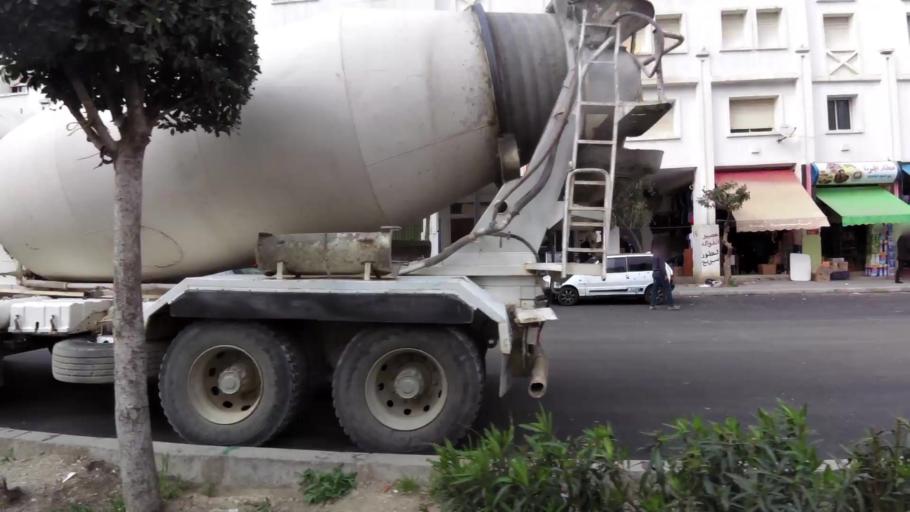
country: MA
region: Tanger-Tetouan
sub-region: Tanger-Assilah
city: Boukhalef
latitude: 35.7373
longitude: -5.8845
